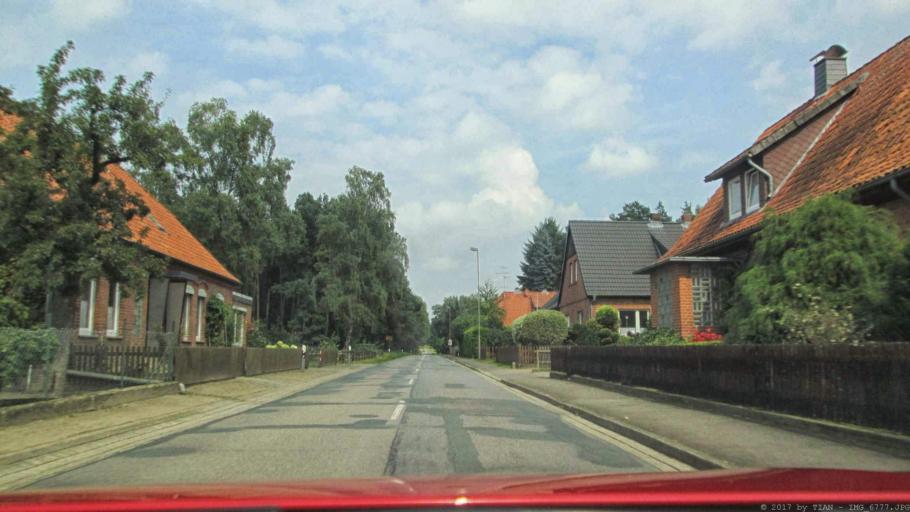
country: DE
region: Lower Saxony
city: Bad Bevensen
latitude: 53.0489
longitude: 10.6046
